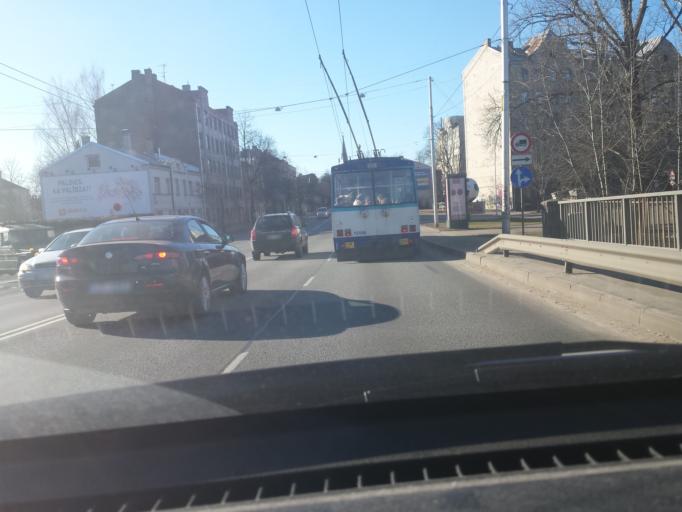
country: LV
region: Riga
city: Riga
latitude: 56.9531
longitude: 24.1571
